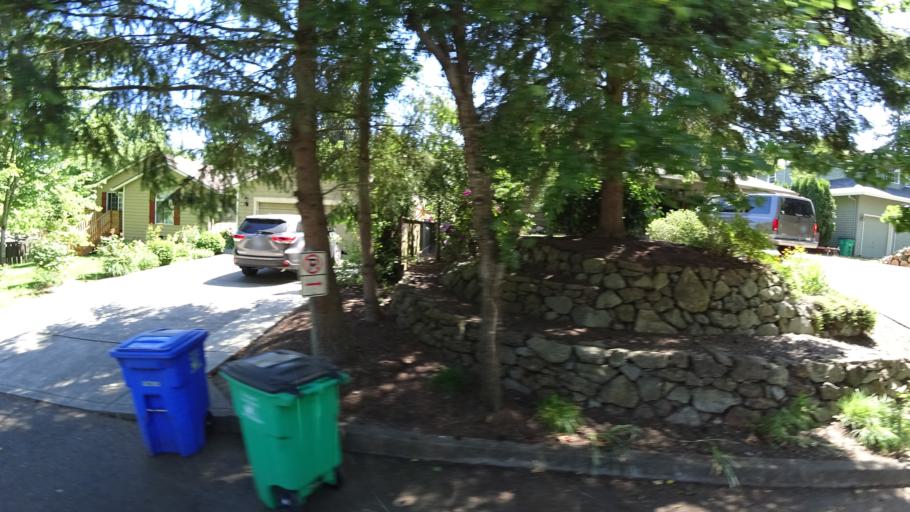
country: US
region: Oregon
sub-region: Washington County
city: Metzger
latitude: 45.4461
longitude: -122.7161
